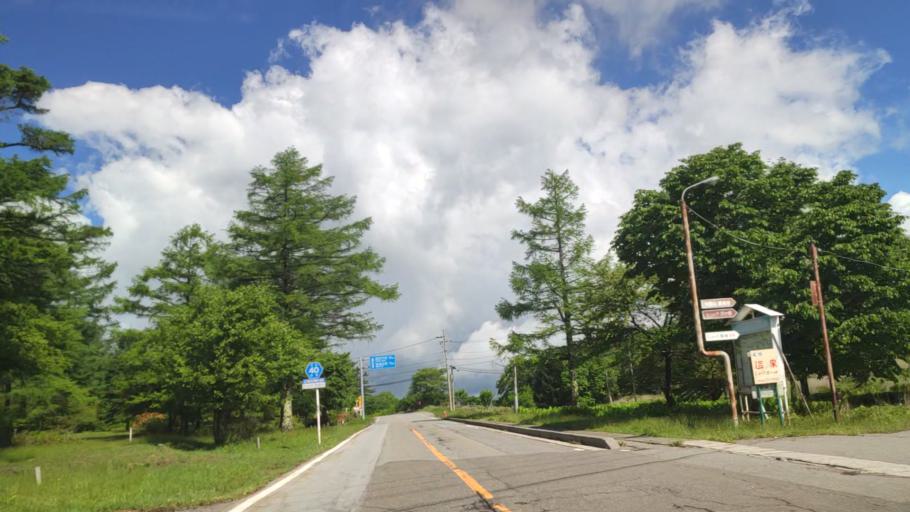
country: JP
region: Nagano
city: Suwa
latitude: 36.0995
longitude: 138.1585
